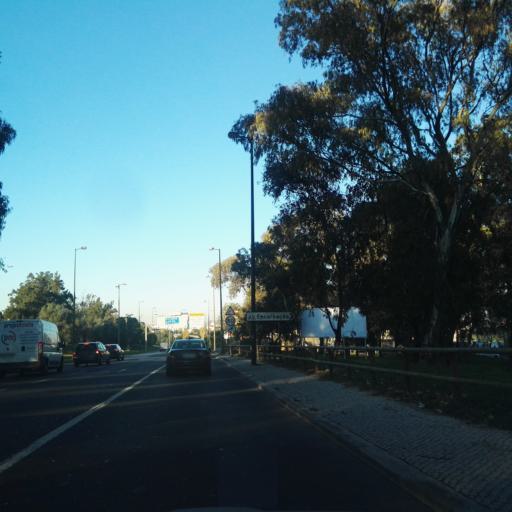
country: PT
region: Lisbon
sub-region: Loures
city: Moscavide
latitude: 38.7764
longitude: -9.1230
